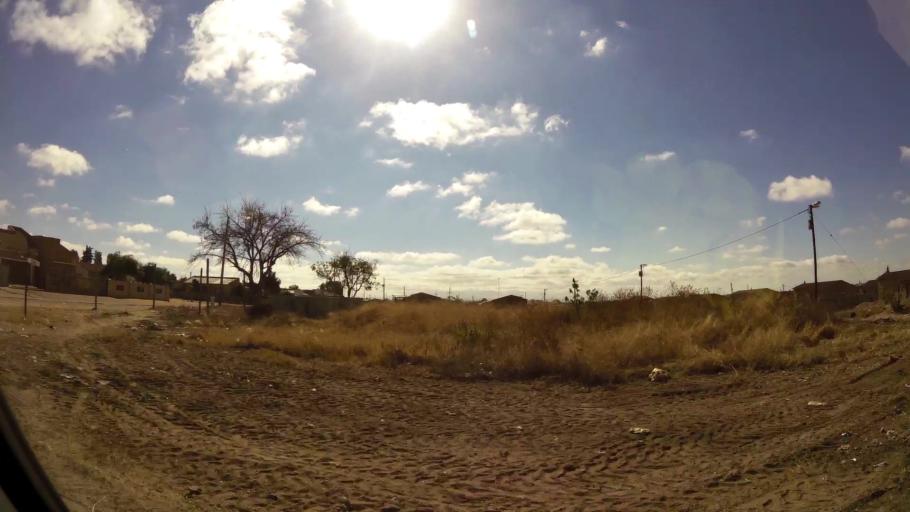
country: ZA
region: Limpopo
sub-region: Capricorn District Municipality
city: Polokwane
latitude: -23.8619
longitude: 29.3952
